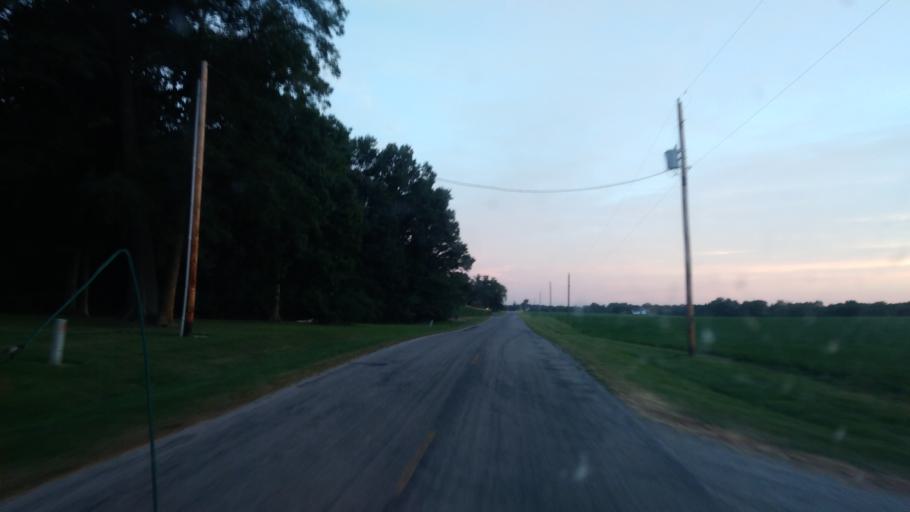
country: US
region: Indiana
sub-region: Wells County
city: Bluffton
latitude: 40.6747
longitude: -85.1298
